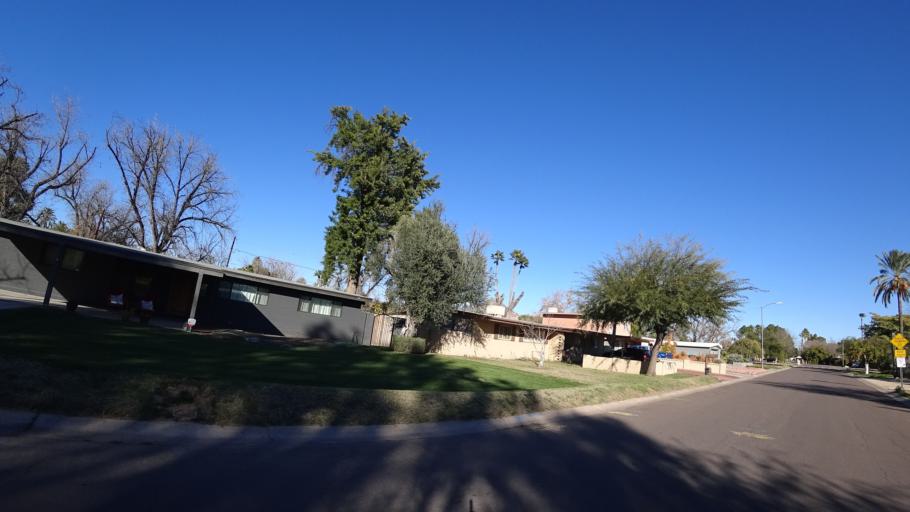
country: US
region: Arizona
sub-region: Maricopa County
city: Phoenix
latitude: 33.5215
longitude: -112.0516
